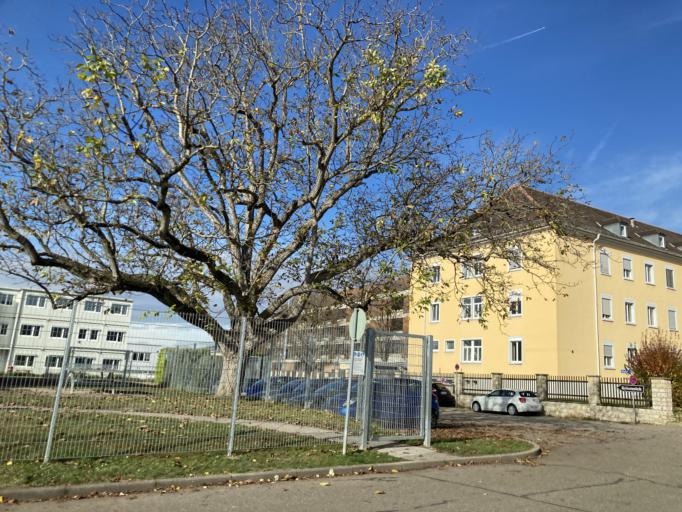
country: DE
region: Baden-Wuerttemberg
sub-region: Freiburg Region
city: Mullheim
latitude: 47.8144
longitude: 7.6210
